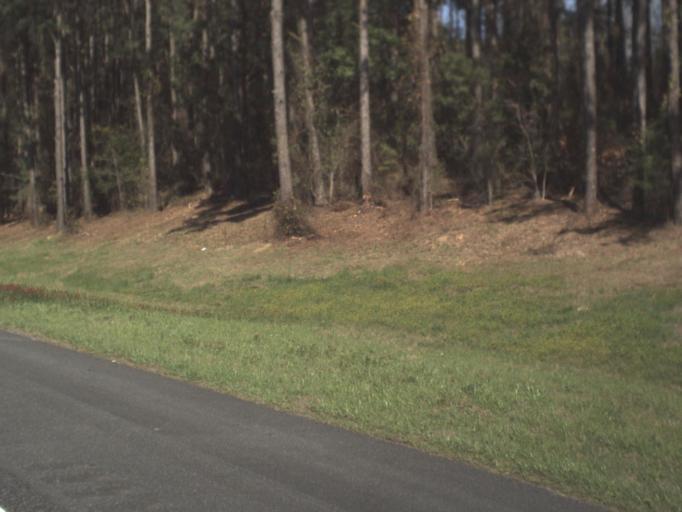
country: US
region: Florida
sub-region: Leon County
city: Tallahassee
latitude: 30.4984
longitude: -84.2013
